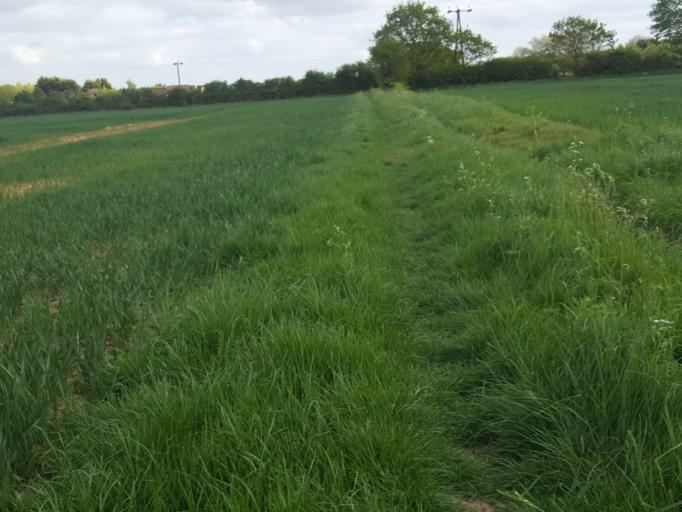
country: GB
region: England
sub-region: Essex
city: Frinton-on-Sea
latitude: 51.8381
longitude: 1.2068
